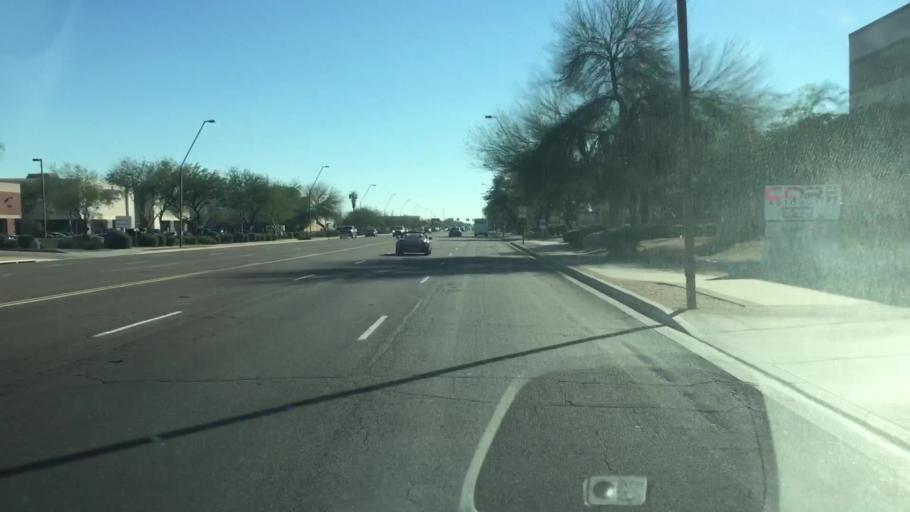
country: US
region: Arizona
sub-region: Maricopa County
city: Guadalupe
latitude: 33.3447
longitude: -111.9632
